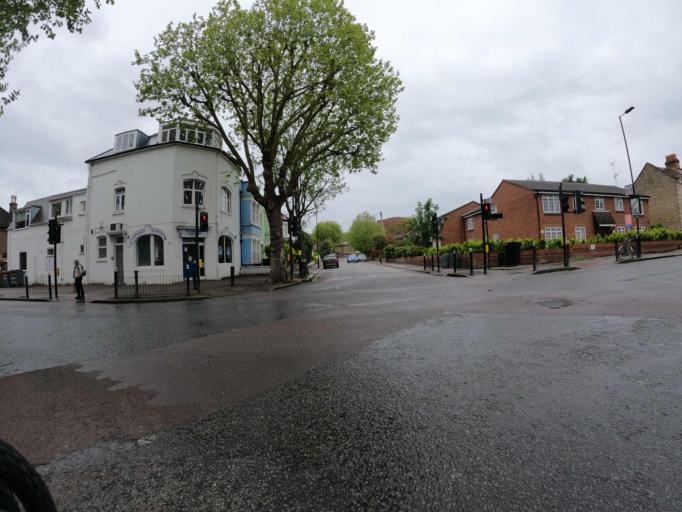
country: GB
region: England
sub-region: Greater London
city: Acton
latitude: 51.5048
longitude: -0.2672
